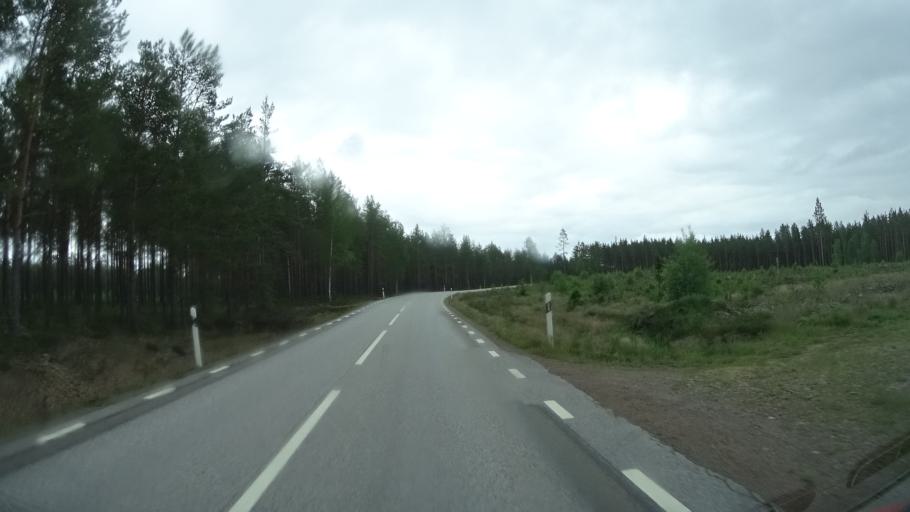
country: SE
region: Kalmar
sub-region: Hultsfreds Kommun
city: Hultsfred
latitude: 57.5269
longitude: 15.7928
